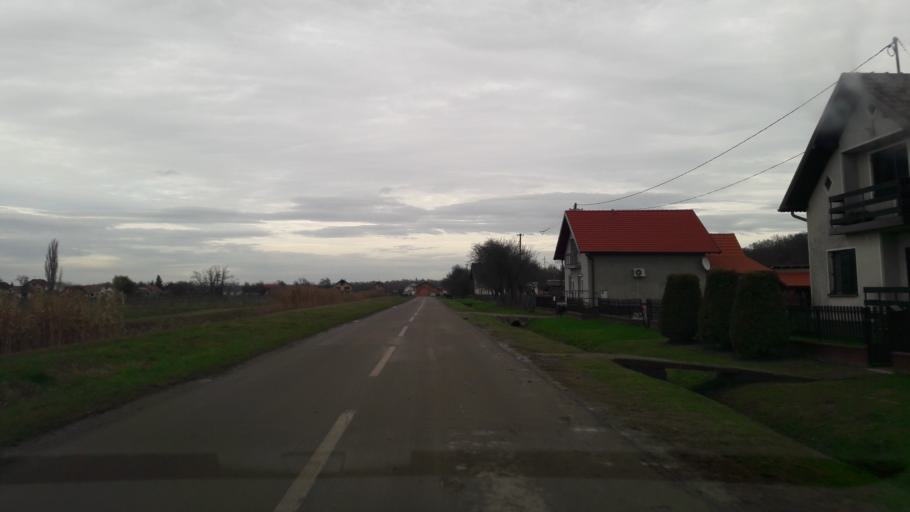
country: HR
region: Osjecko-Baranjska
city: Velimirovac
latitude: 45.6134
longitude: 18.0660
